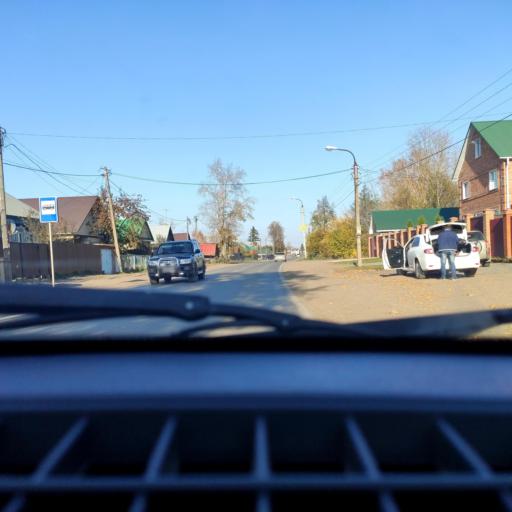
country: RU
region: Bashkortostan
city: Ufa
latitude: 54.8163
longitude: 56.1667
